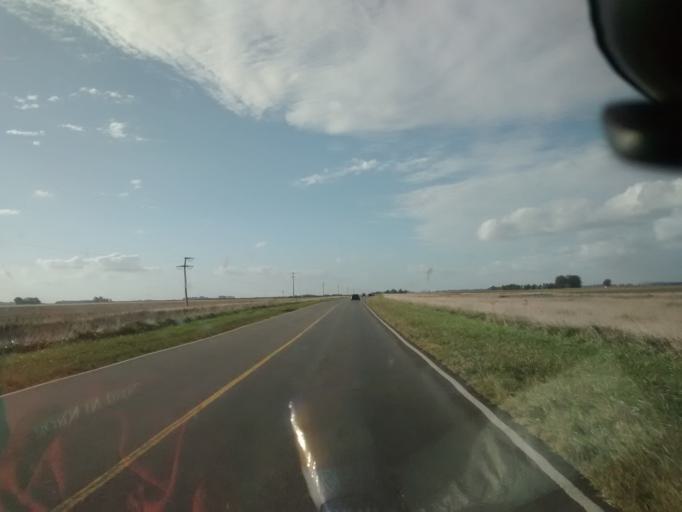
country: AR
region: Buenos Aires
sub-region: Partido de Ayacucho
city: Ayacucho
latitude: -36.7370
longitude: -58.5708
